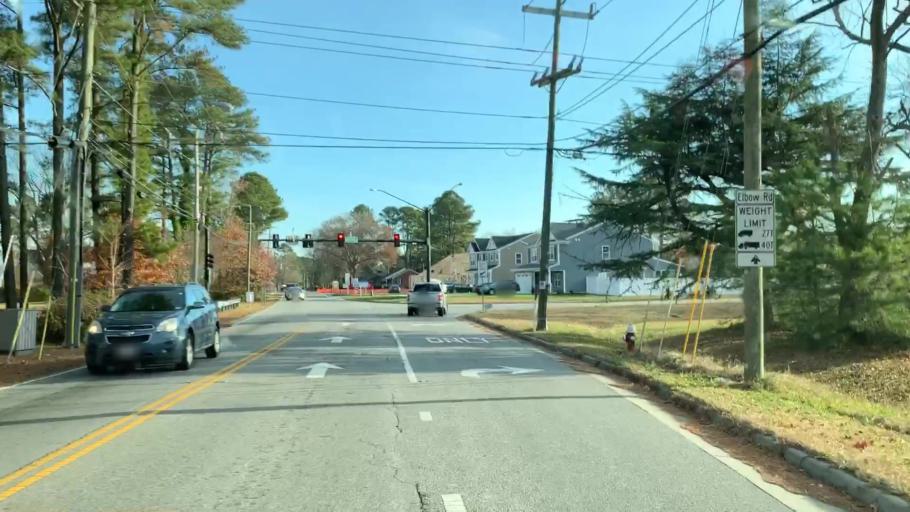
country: US
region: Virginia
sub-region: City of Chesapeake
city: Chesapeake
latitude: 36.7612
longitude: -76.1405
